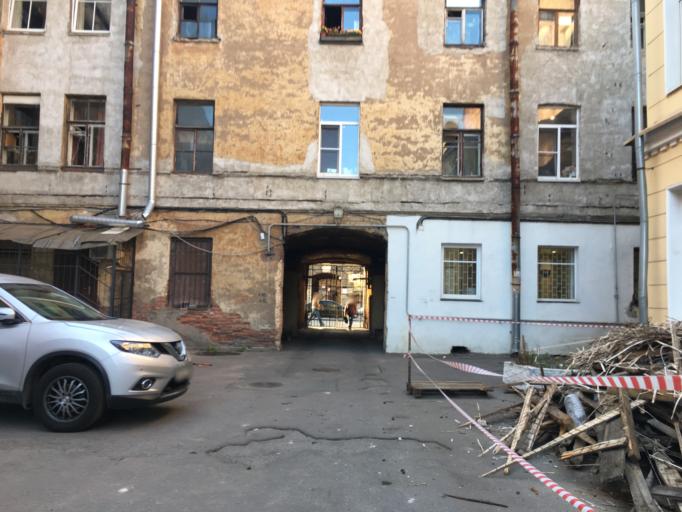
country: RU
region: St.-Petersburg
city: Centralniy
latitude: 59.9200
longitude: 30.3419
